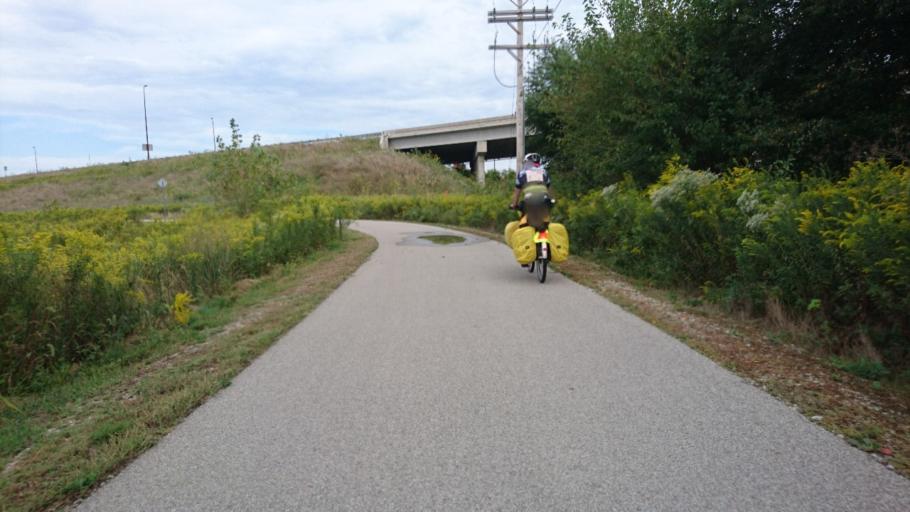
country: US
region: Illinois
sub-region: Sangamon County
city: Southern View
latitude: 39.7431
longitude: -89.6725
